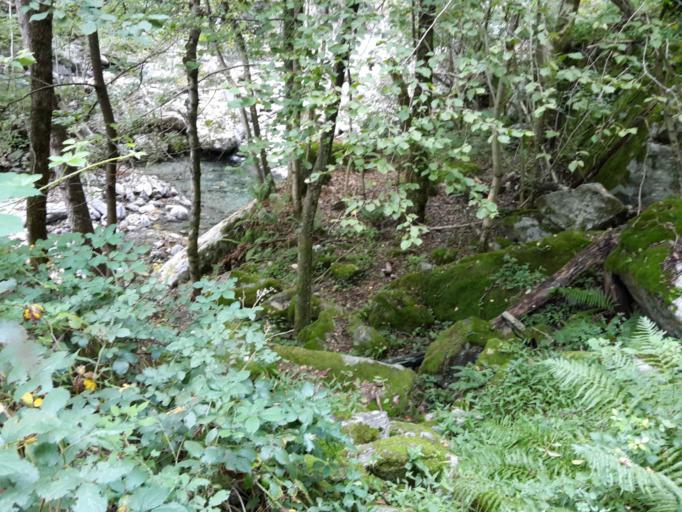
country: CH
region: Ticino
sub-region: Bellinzona District
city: Sementina
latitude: 46.1912
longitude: 8.9840
